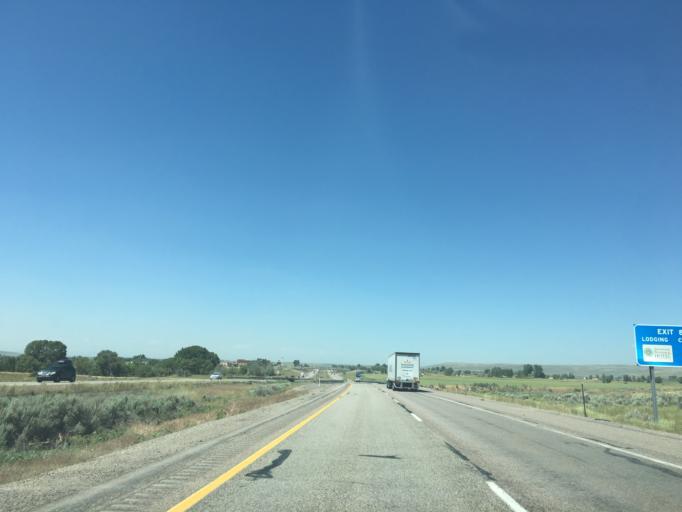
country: US
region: Idaho
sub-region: Bingham County
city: Fort Hall
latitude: 43.0102
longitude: -112.4081
